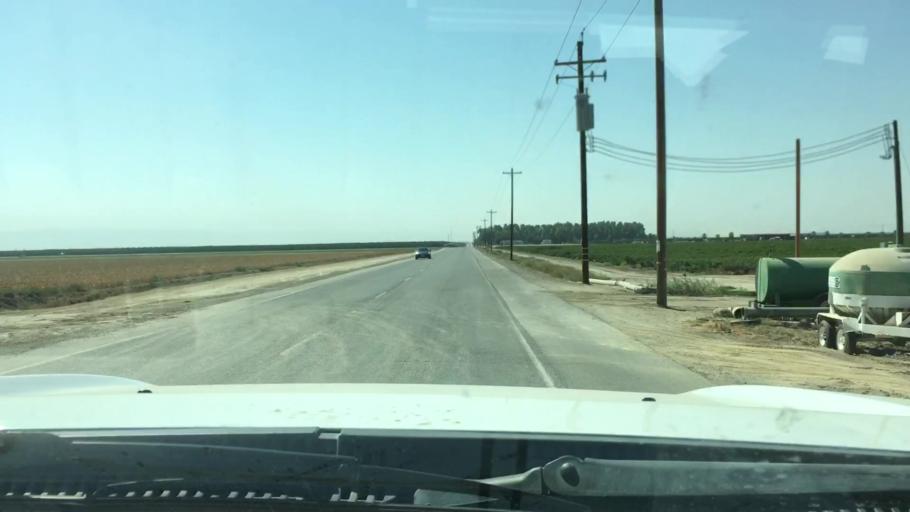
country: US
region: California
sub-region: Kern County
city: Buttonwillow
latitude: 35.5005
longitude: -119.4617
